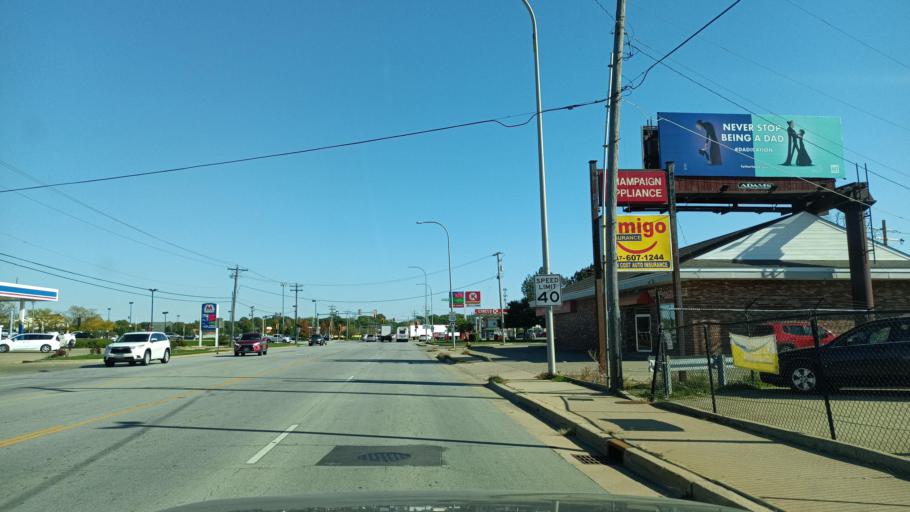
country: US
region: Illinois
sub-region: Champaign County
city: Champaign
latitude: 40.1330
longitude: -88.2600
